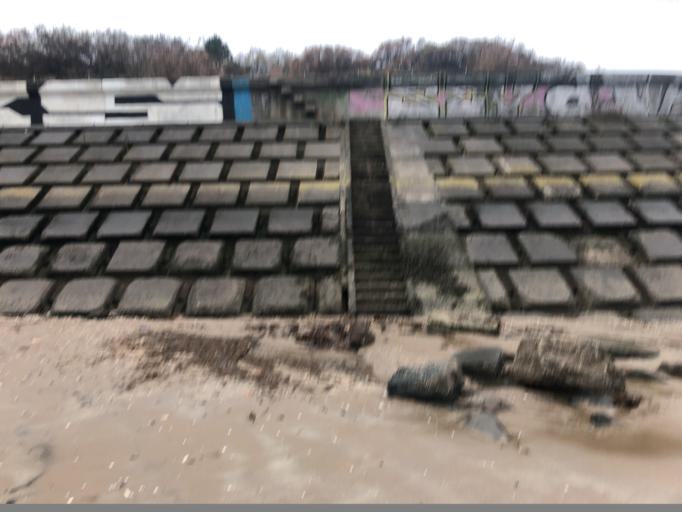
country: GB
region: Scotland
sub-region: West Lothian
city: Seafield
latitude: 55.9692
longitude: -3.1370
